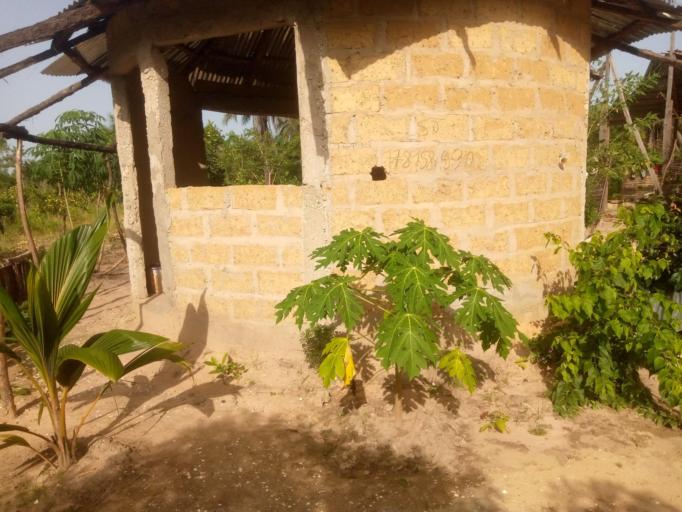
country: GM
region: Western
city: Gunjur
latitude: 13.0304
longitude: -16.7272
